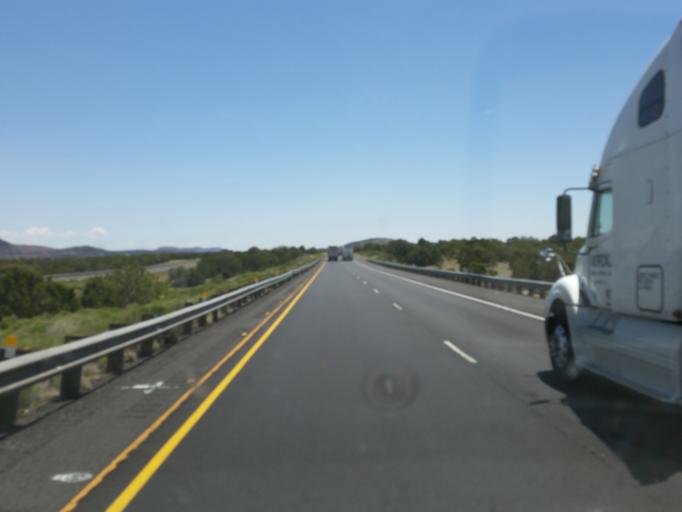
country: US
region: Arizona
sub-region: Coconino County
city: Flagstaff
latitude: 35.2020
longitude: -111.4547
